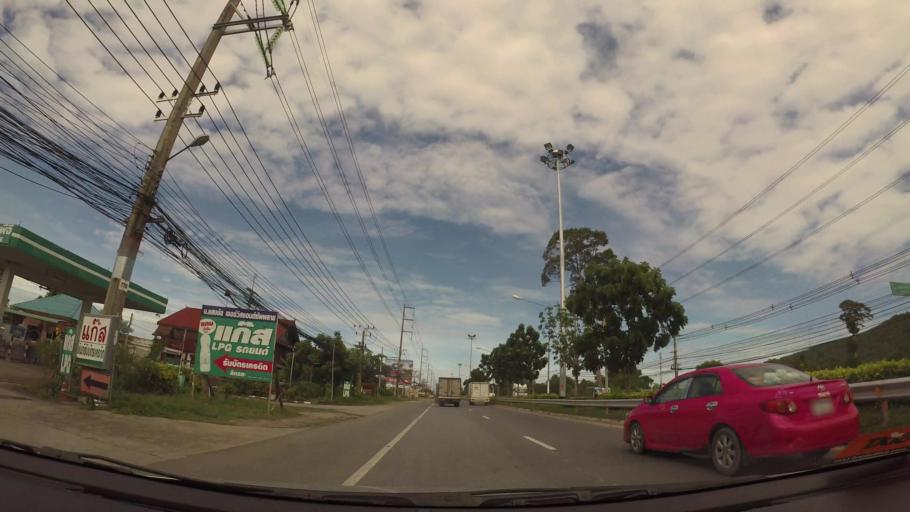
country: TH
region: Rayong
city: Ban Chang
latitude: 12.7483
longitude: 101.1032
